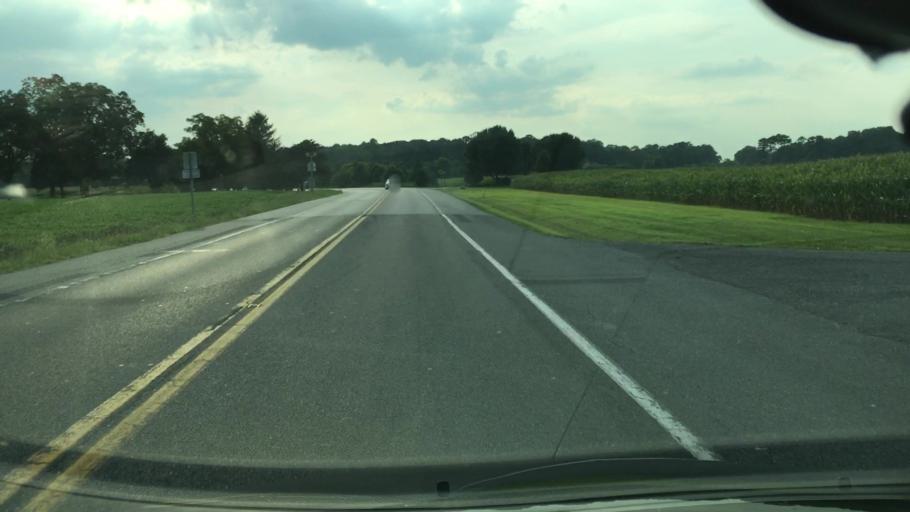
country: US
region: Maryland
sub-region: Worcester County
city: Ocean Pines
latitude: 38.3908
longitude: -75.1982
